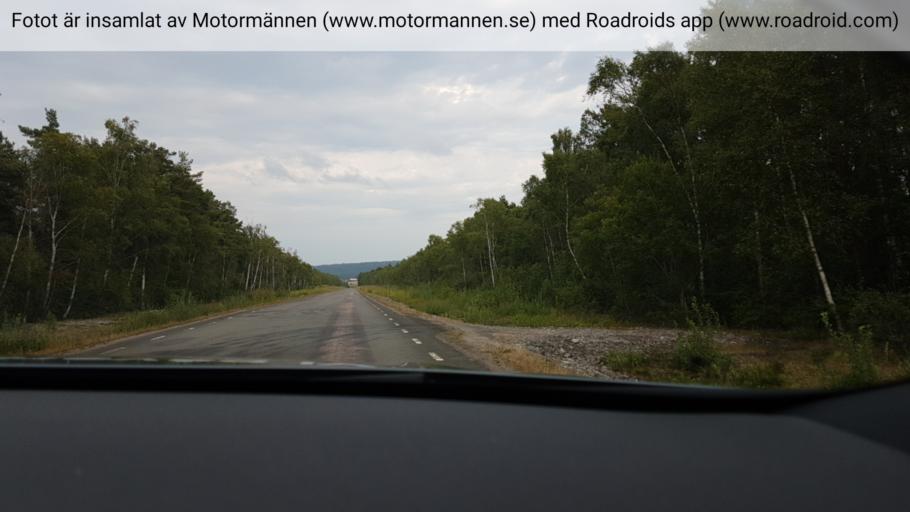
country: SE
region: Vaestra Goetaland
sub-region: Falkopings Kommun
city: Akarp
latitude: 58.1780
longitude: 13.6551
